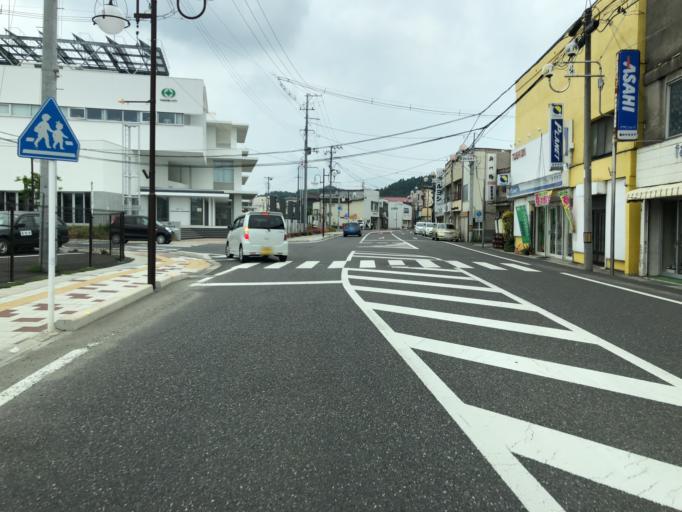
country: JP
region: Fukushima
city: Funehikimachi-funehiki
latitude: 37.4410
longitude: 140.5755
